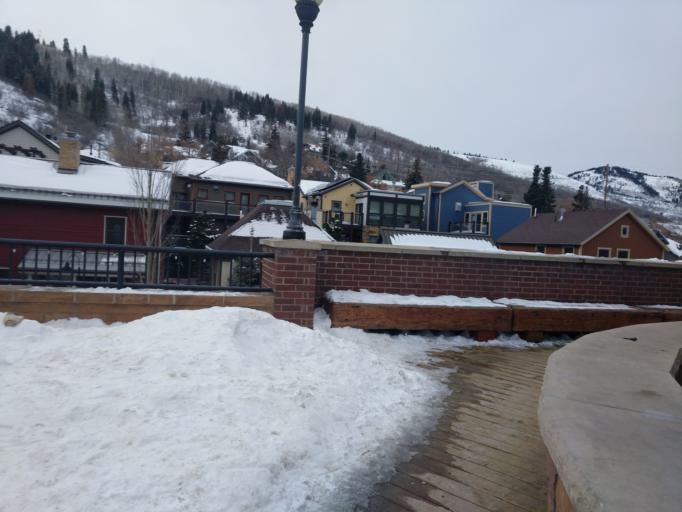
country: US
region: Utah
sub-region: Summit County
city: Park City
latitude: 40.6475
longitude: -111.4988
